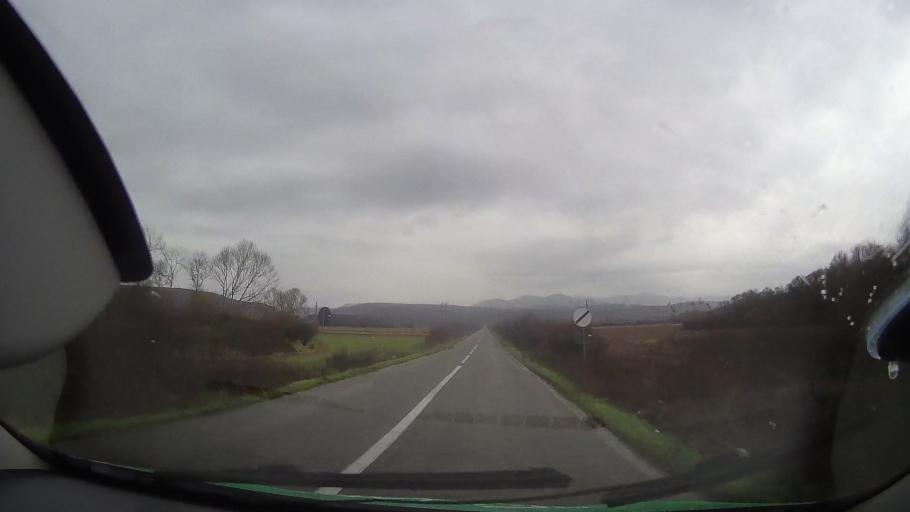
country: RO
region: Bihor
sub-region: Comuna Soimi
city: Soimi
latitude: 46.6946
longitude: 22.0953
